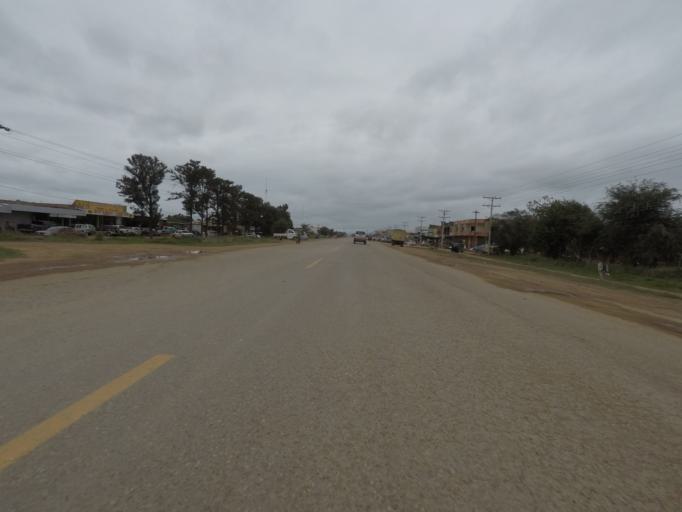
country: BO
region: Santa Cruz
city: Okinawa Numero Uno
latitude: -17.2635
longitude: -62.5554
